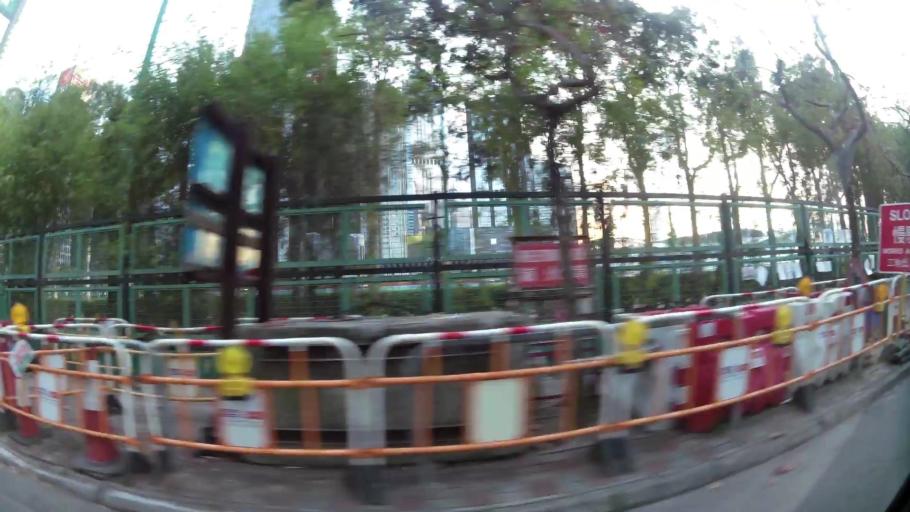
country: HK
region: Wanchai
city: Wan Chai
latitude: 22.2814
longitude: 114.1786
